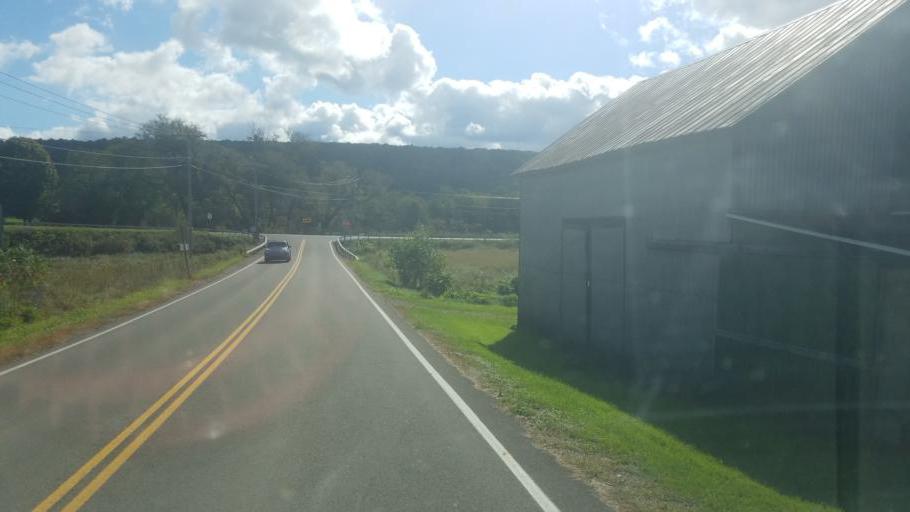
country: US
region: New York
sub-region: Allegany County
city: Cuba
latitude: 42.2420
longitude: -78.2743
